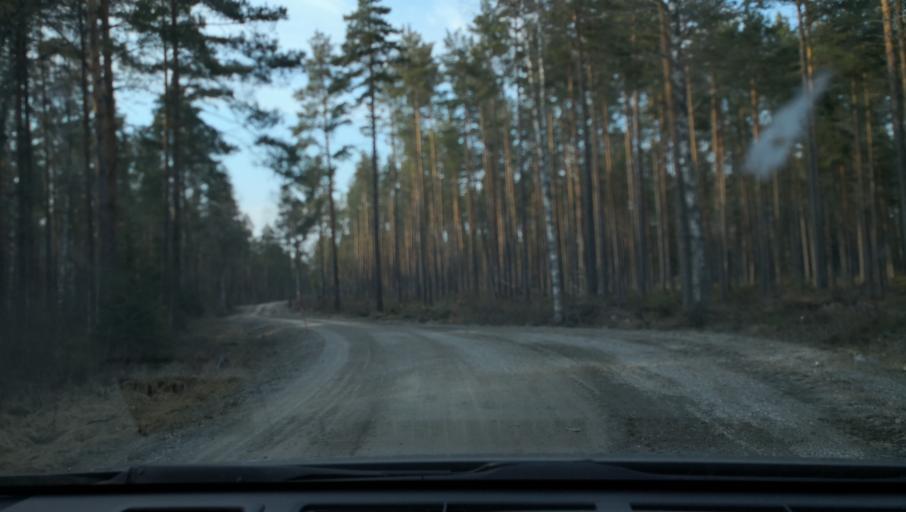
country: SE
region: OErebro
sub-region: Lindesbergs Kommun
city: Frovi
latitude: 59.3627
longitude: 15.3288
